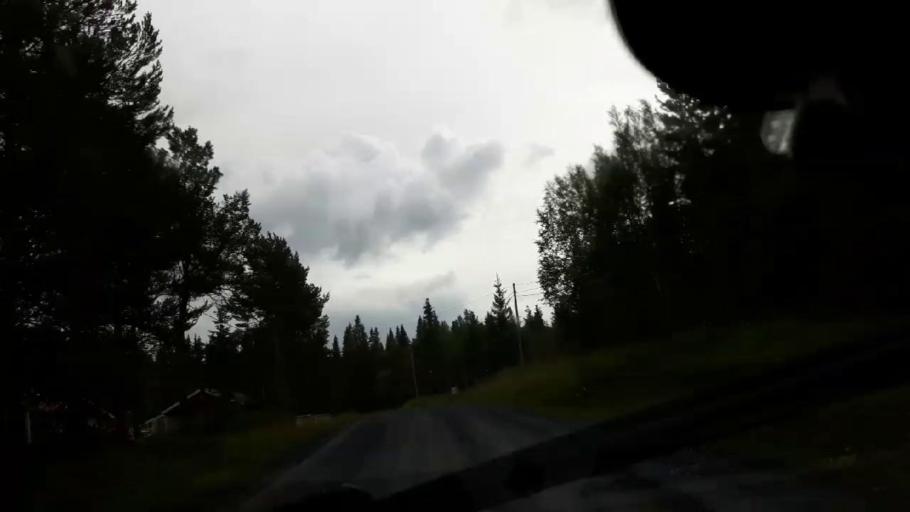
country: SE
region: Jaemtland
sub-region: Krokoms Kommun
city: Valla
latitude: 63.3885
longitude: 13.8781
